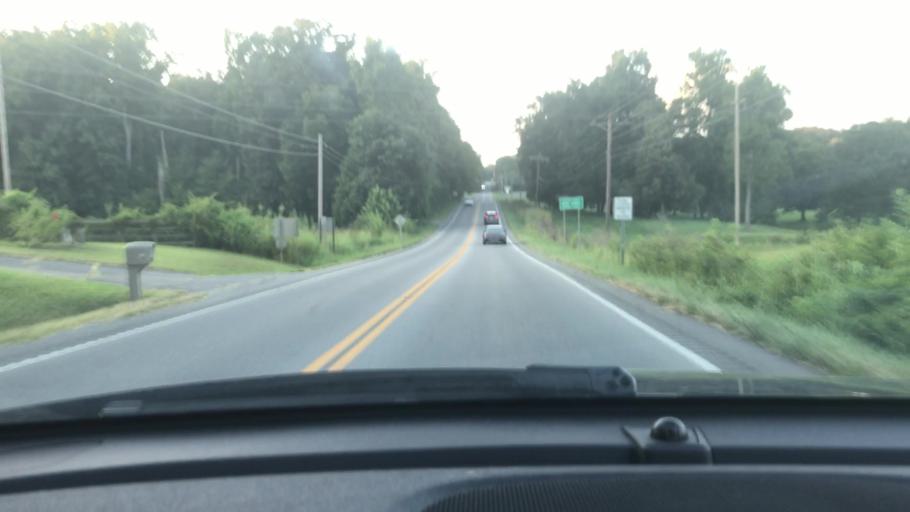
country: US
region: Tennessee
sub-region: Dickson County
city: Dickson
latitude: 36.0964
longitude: -87.3754
